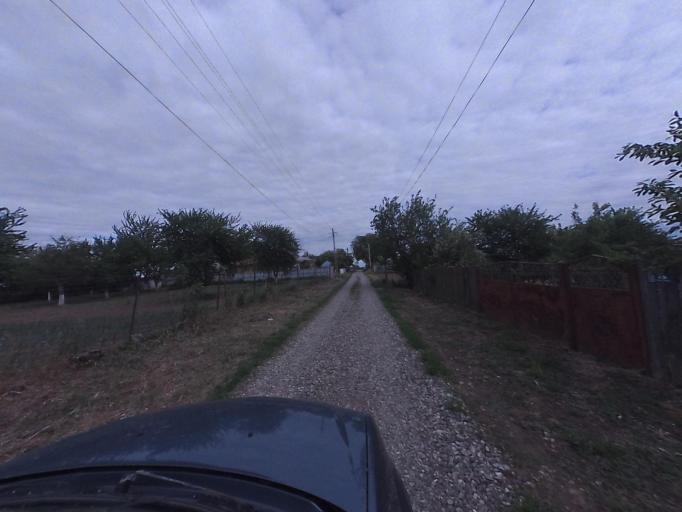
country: RO
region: Neamt
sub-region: Comuna Dulcesti
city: Dulcesti
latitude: 46.9592
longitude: 26.7979
